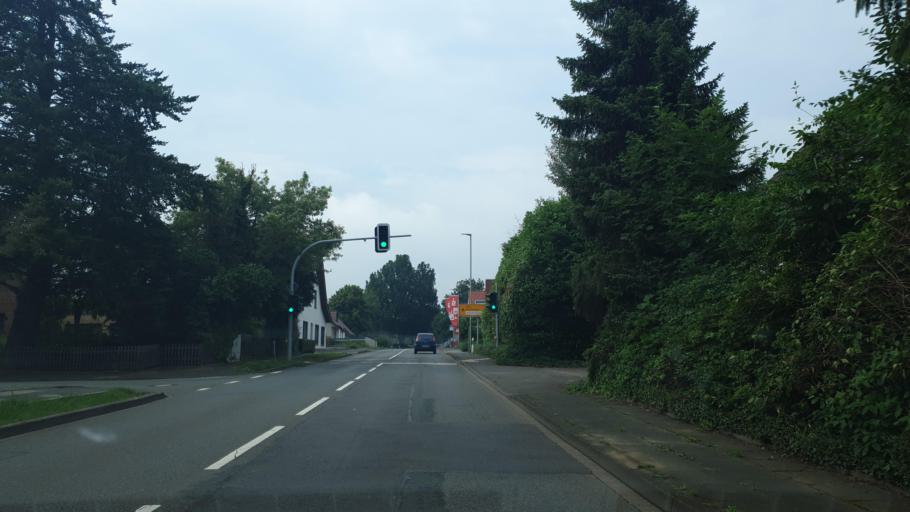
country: DE
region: North Rhine-Westphalia
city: Bad Oeynhausen
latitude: 52.2502
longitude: 8.7824
